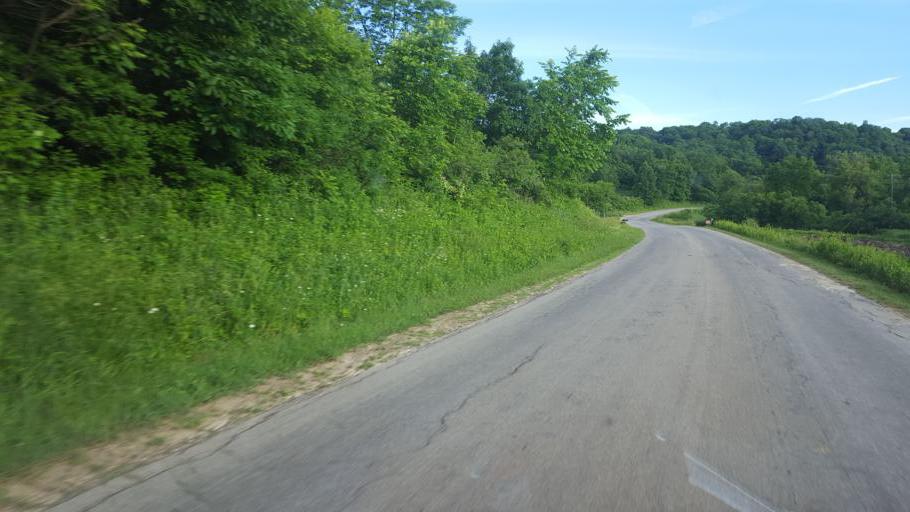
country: US
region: Wisconsin
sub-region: Vernon County
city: Hillsboro
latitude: 43.5975
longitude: -90.3678
